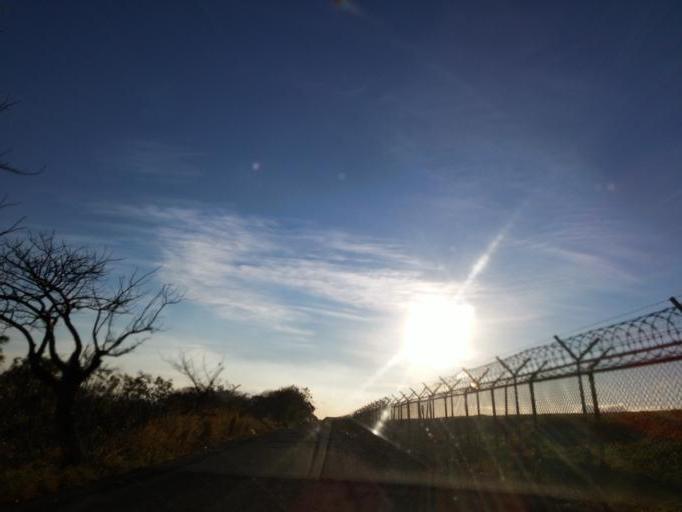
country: CR
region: Alajuela
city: Alajuela
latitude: 9.9944
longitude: -84.2046
